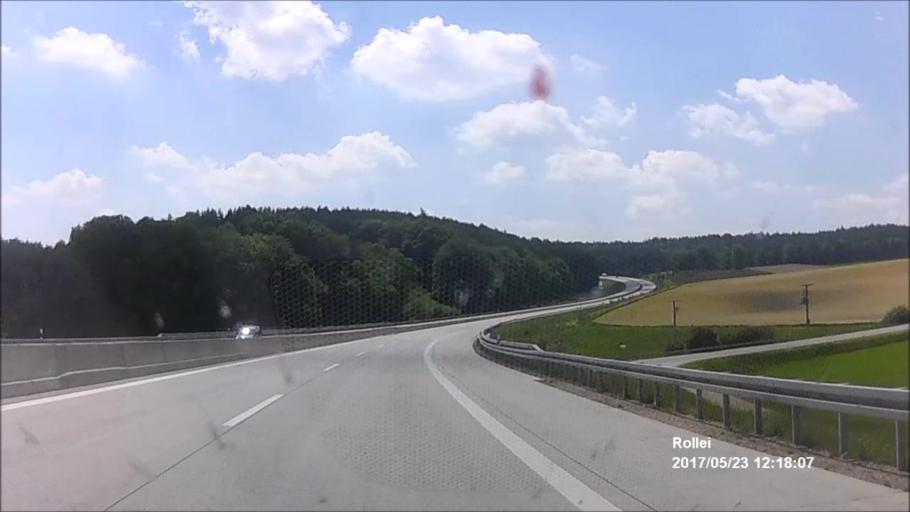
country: DE
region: Bavaria
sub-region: Upper Palatinate
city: Schierling
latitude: 48.7760
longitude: 12.1426
